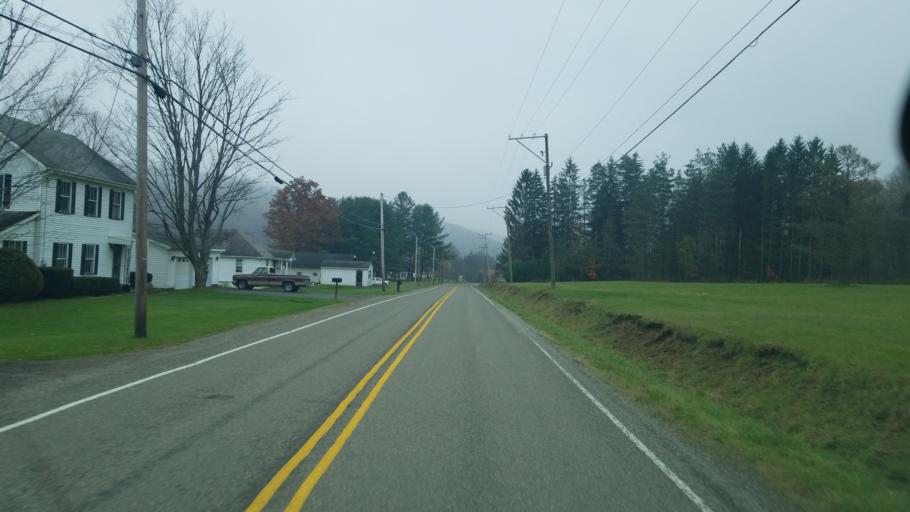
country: US
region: Pennsylvania
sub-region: McKean County
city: Smethport
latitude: 41.8874
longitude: -78.4994
